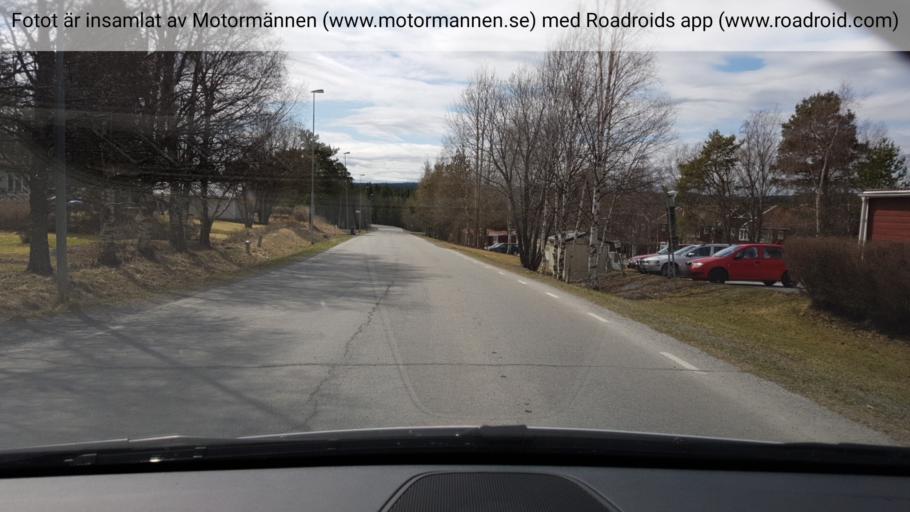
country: SE
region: Jaemtland
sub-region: OEstersunds Kommun
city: Brunflo
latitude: 63.0744
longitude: 14.8198
